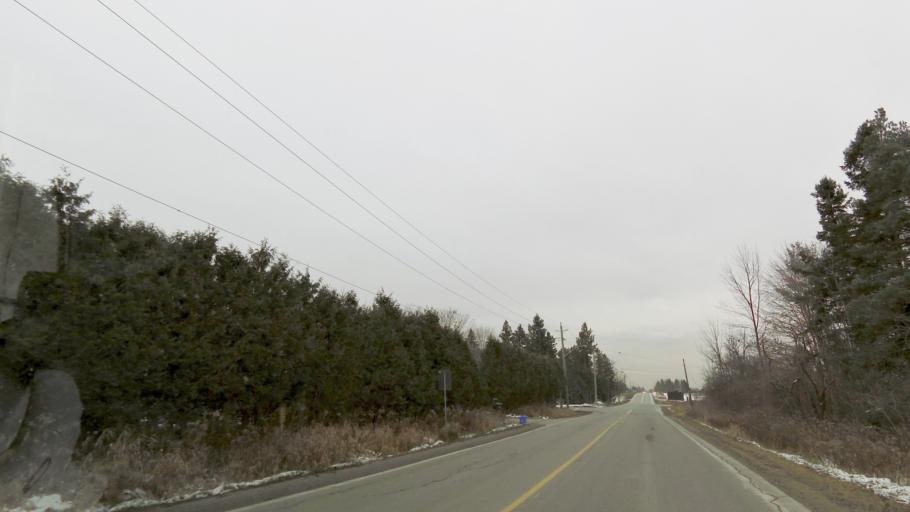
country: CA
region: Ontario
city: Vaughan
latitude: 43.8588
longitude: -79.5908
